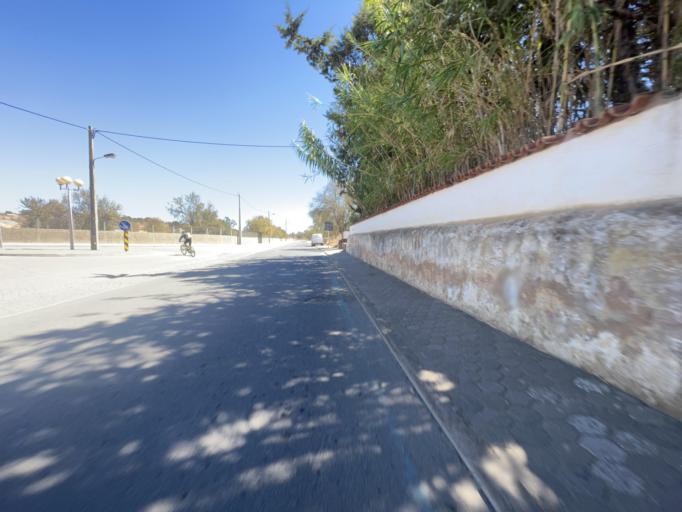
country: PT
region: Faro
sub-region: Portimao
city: Portimao
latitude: 37.1254
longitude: -8.5124
